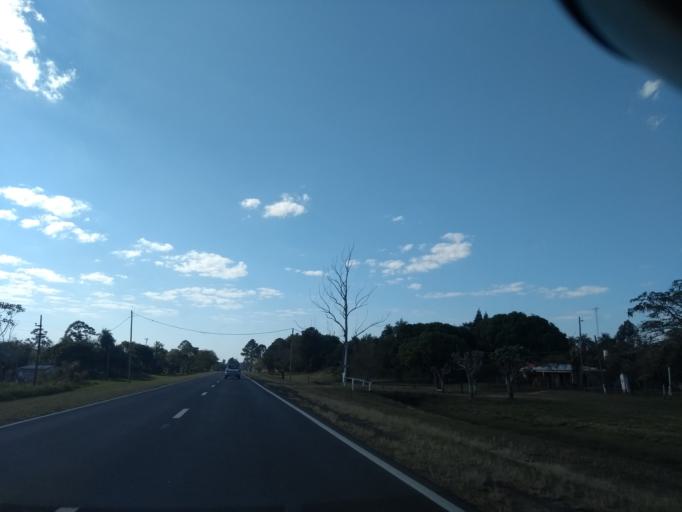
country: AR
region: Corrientes
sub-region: Departamento de Itati
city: Itati
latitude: -27.3661
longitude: -58.3101
